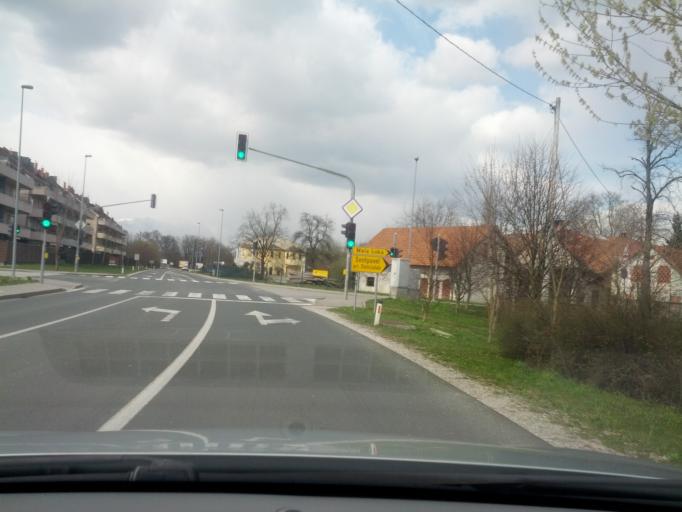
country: SI
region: Dol pri Ljubljani
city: Dol pri Ljubljani
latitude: 46.1053
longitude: 14.5928
